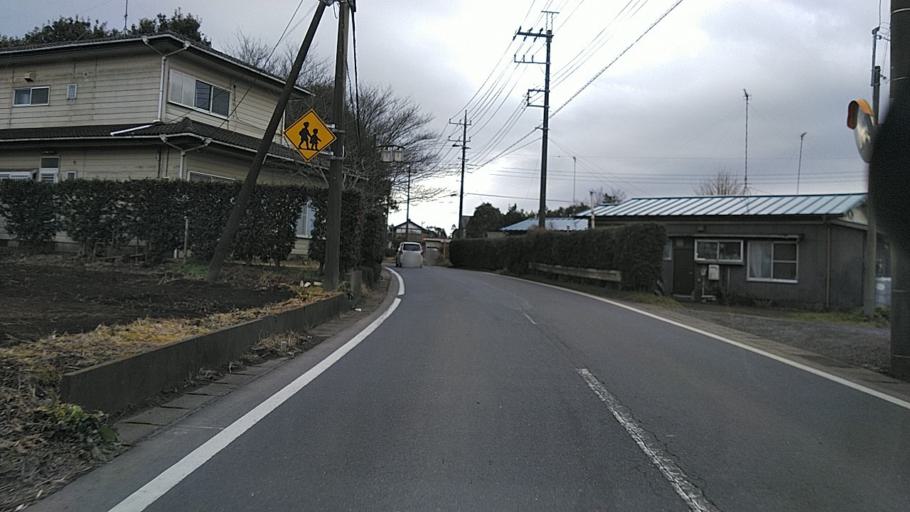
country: JP
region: Chiba
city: Sawara
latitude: 35.8411
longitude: 140.4550
